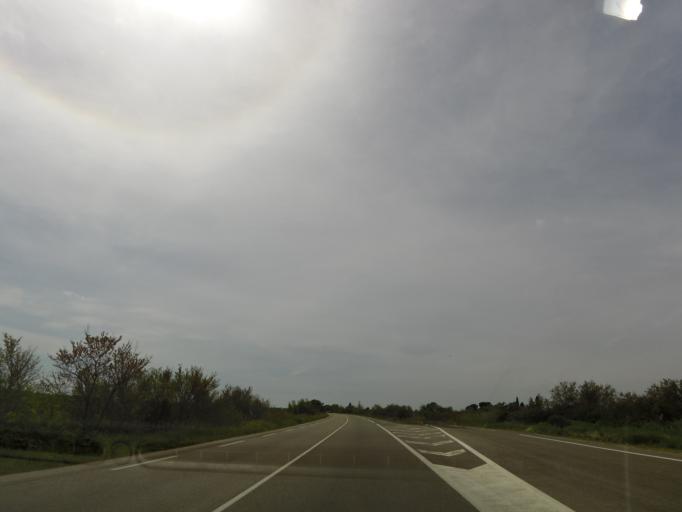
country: FR
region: Languedoc-Roussillon
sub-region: Departement de l'Herault
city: Saint-Just
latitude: 43.6174
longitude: 4.1141
